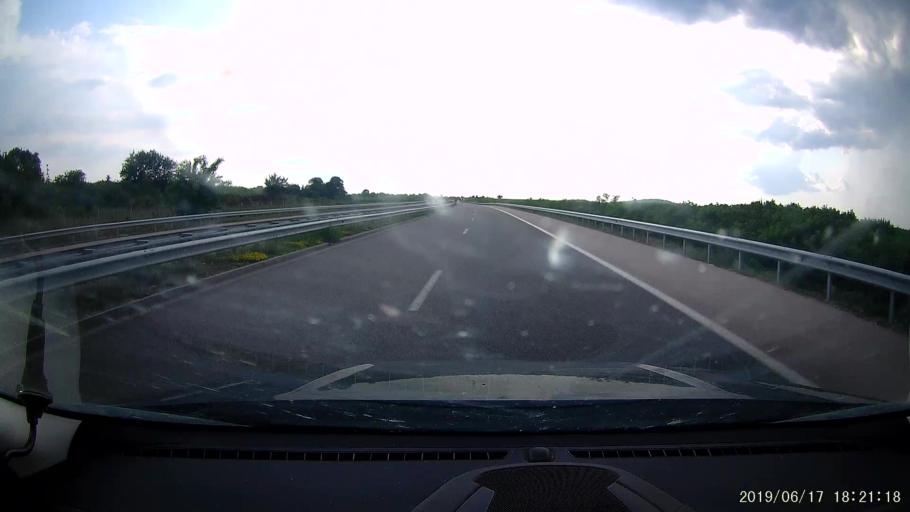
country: BG
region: Khaskovo
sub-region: Obshtina Simeonovgrad
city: Simeonovgrad
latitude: 41.9675
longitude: 25.7874
